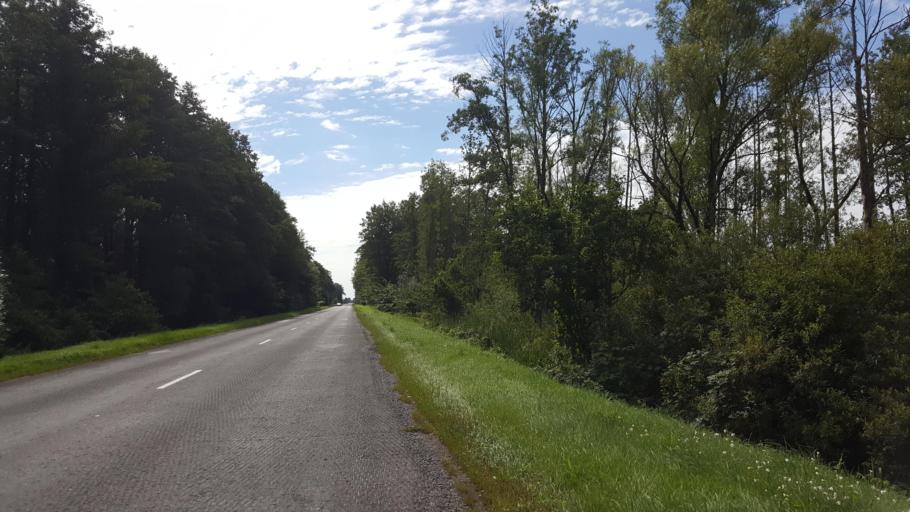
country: BY
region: Brest
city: Zhabinka
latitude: 52.2705
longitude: 23.9557
